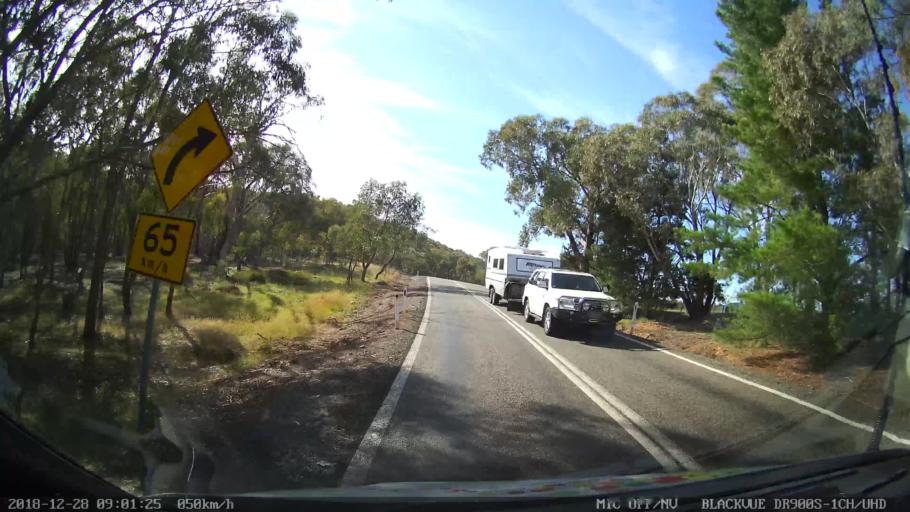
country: AU
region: New South Wales
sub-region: Upper Lachlan Shire
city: Crookwell
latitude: -34.1462
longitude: 149.3335
